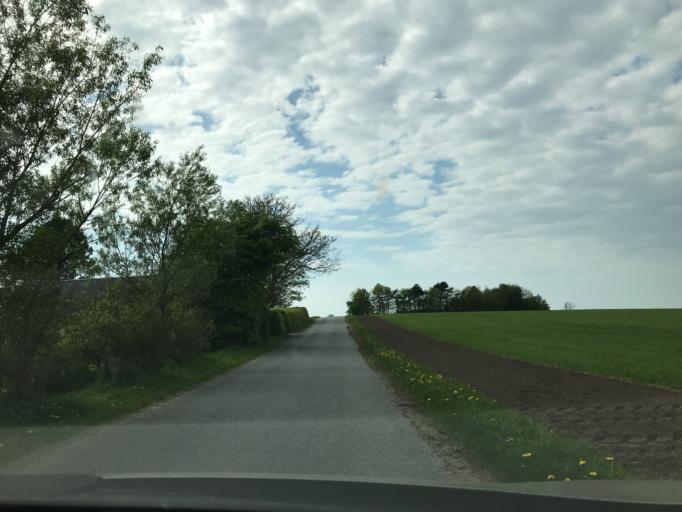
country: DK
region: South Denmark
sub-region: Middelfart Kommune
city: Ejby
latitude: 55.3622
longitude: 9.8543
